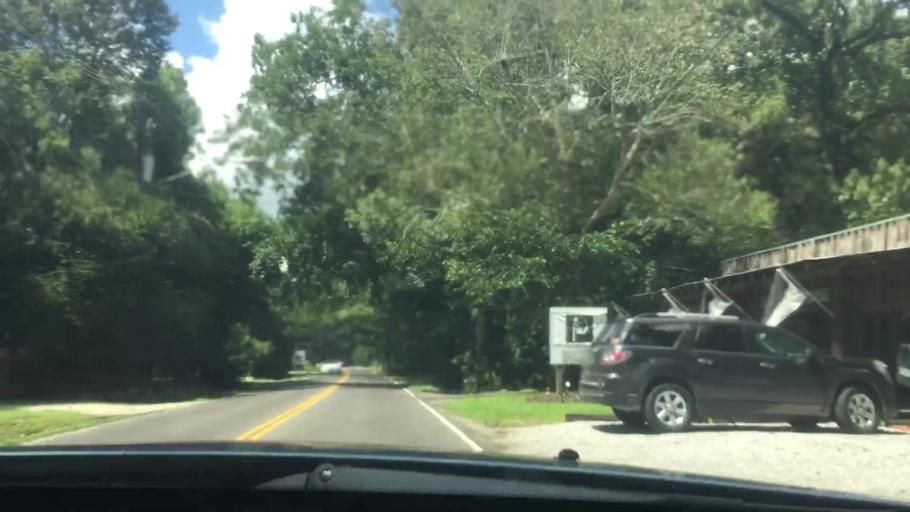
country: US
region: Louisiana
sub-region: East Baton Rouge Parish
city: Gardere
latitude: 30.3696
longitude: -91.1237
